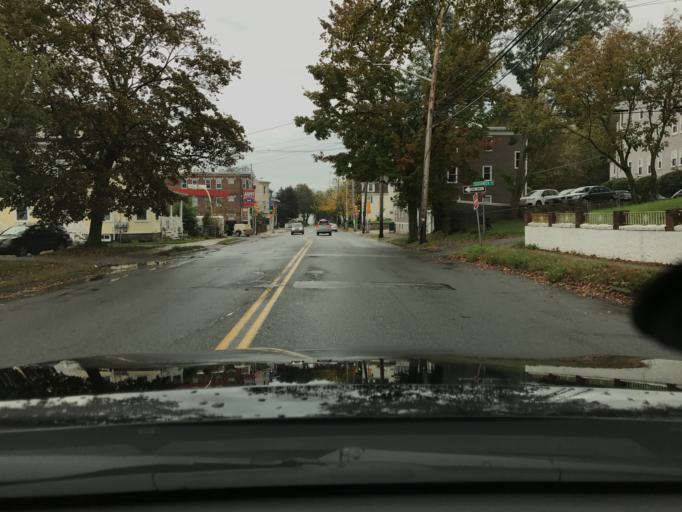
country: US
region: Massachusetts
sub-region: Essex County
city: Peabody
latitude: 42.5303
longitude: -70.9365
